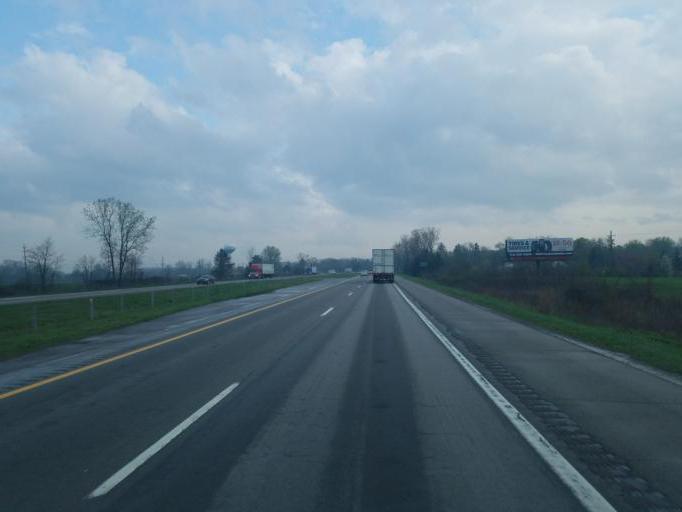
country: US
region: Michigan
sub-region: Washtenaw County
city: Milan
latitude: 42.0930
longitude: -83.6749
